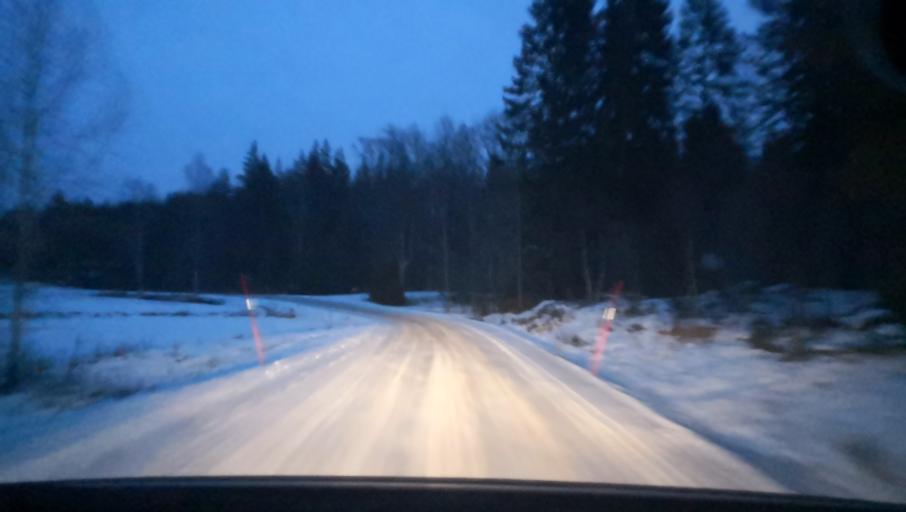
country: SE
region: Uppsala
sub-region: Heby Kommun
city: Tarnsjo
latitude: 60.2411
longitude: 16.7000
